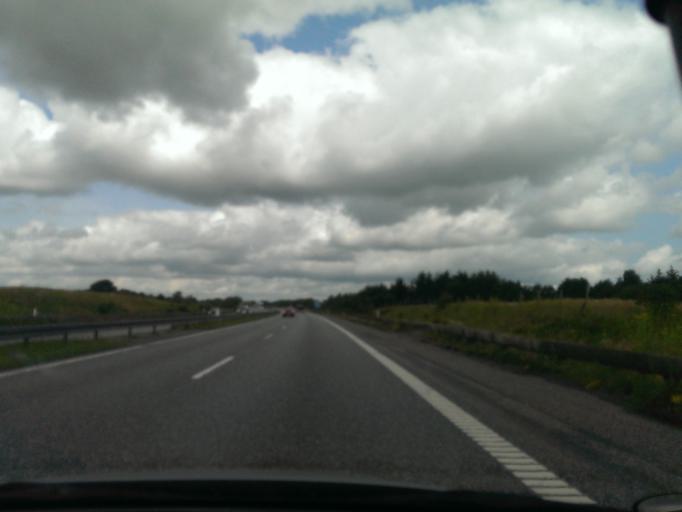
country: DK
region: North Denmark
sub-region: Mariagerfjord Kommune
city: Hobro
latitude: 56.5665
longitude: 9.8589
